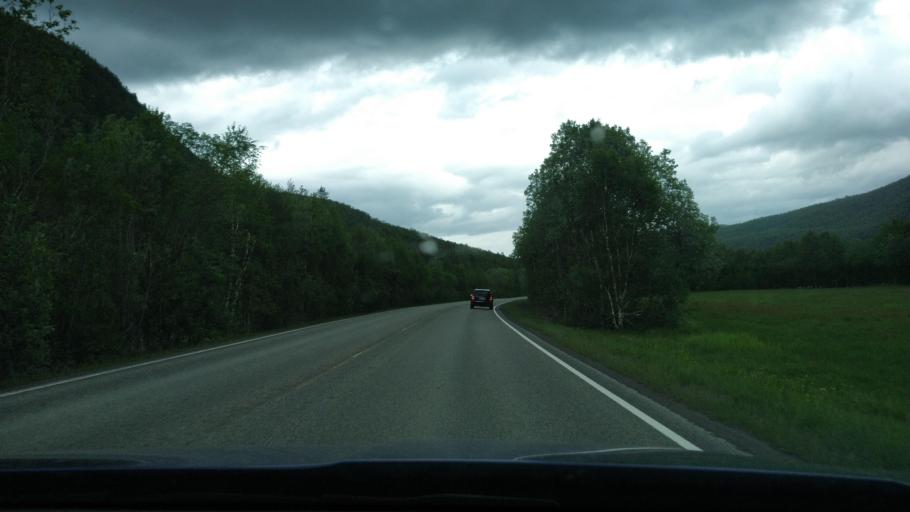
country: NO
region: Troms
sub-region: Bardu
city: Setermoen
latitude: 68.9762
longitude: 18.4996
